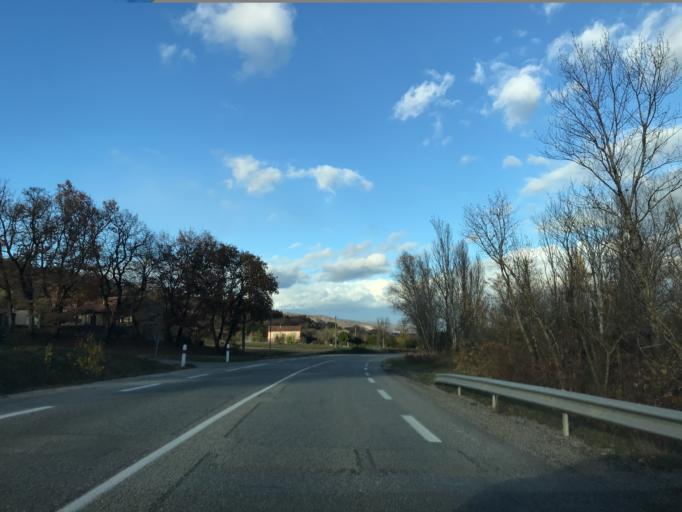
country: FR
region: Rhone-Alpes
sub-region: Departement de l'Ardeche
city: Le Pouzin
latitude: 44.7195
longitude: 4.7342
